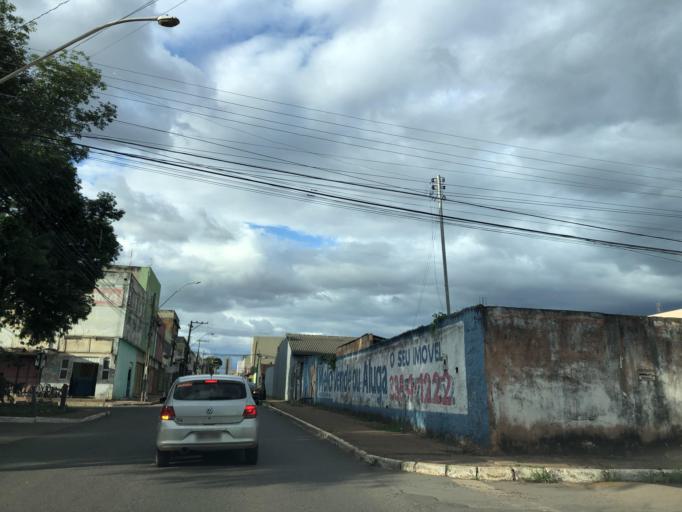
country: BR
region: Goias
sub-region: Luziania
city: Luziania
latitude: -16.0302
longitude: -48.0603
